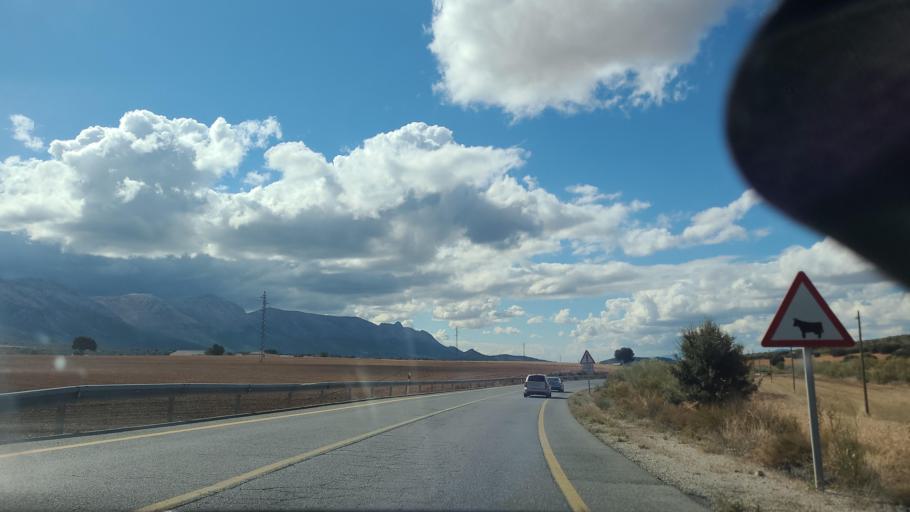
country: ES
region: Andalusia
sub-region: Provincia de Granada
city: Pinar
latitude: 37.4034
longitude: -3.3954
